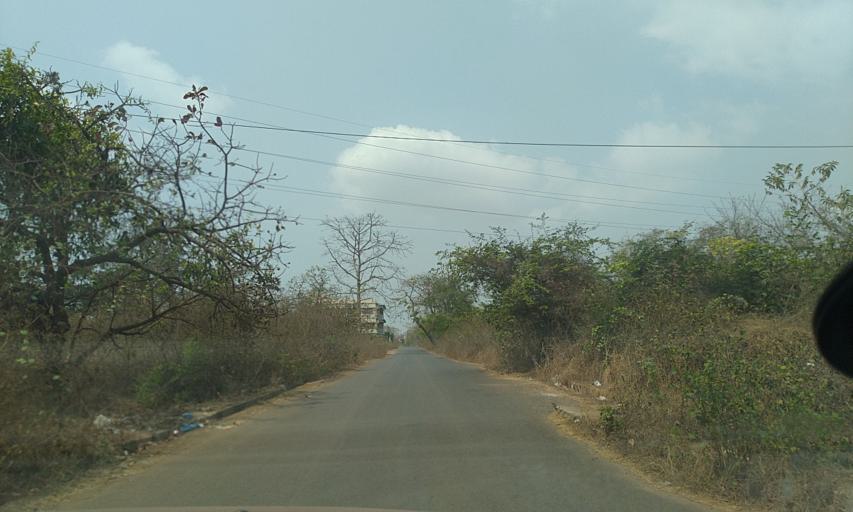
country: IN
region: Goa
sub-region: North Goa
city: Goa Velha
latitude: 15.4857
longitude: 73.9009
